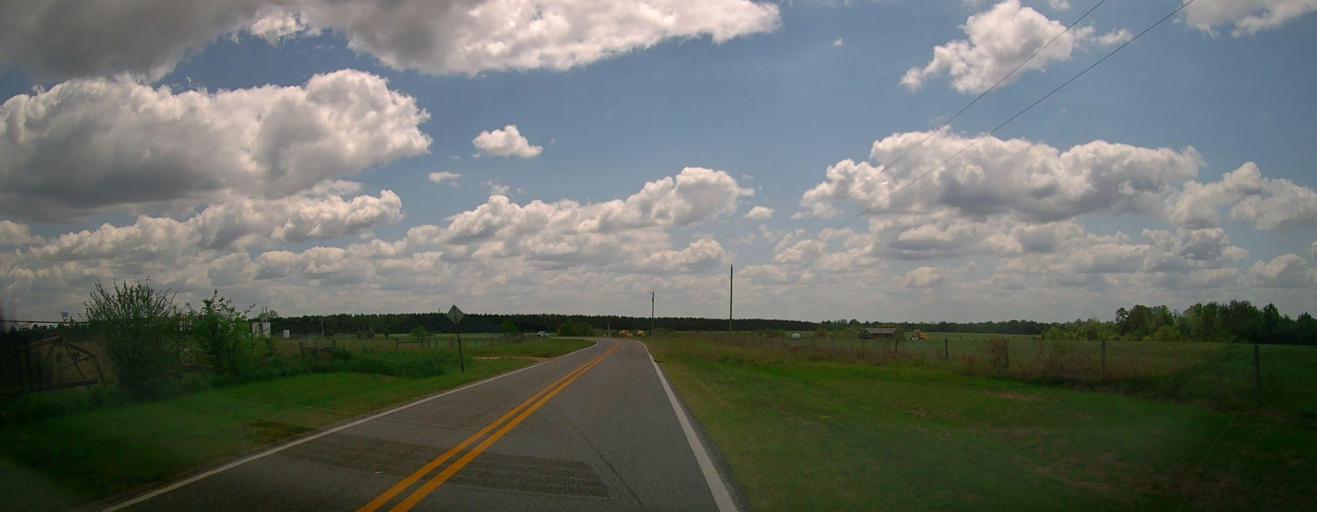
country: US
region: Georgia
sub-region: Laurens County
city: East Dublin
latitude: 32.5475
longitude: -82.8188
